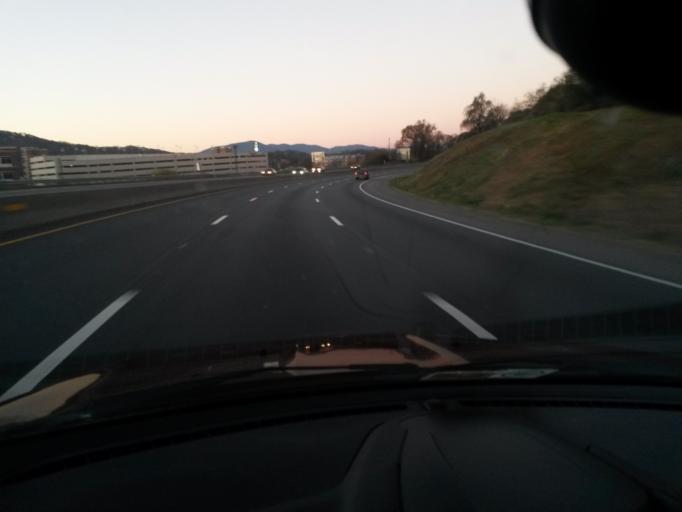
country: US
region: Virginia
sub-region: City of Roanoke
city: Cedar Bluff
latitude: 37.2593
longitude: -79.9424
